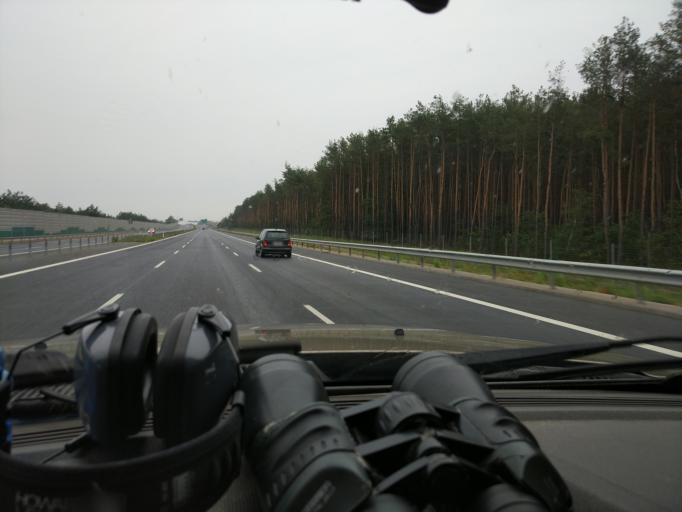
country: PL
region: Masovian Voivodeship
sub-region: Powiat wolominski
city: Radzymin
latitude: 52.3848
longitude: 21.1927
